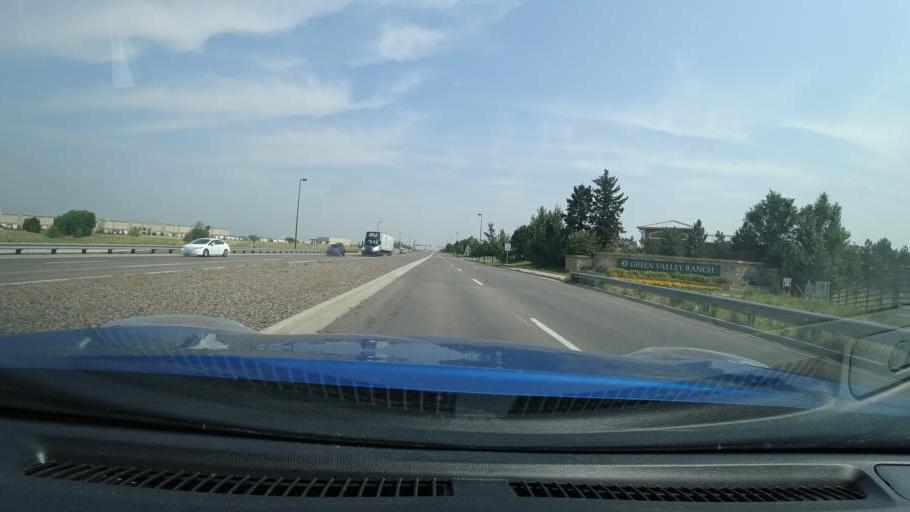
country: US
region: Colorado
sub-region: Adams County
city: Aurora
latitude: 39.7712
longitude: -104.7721
